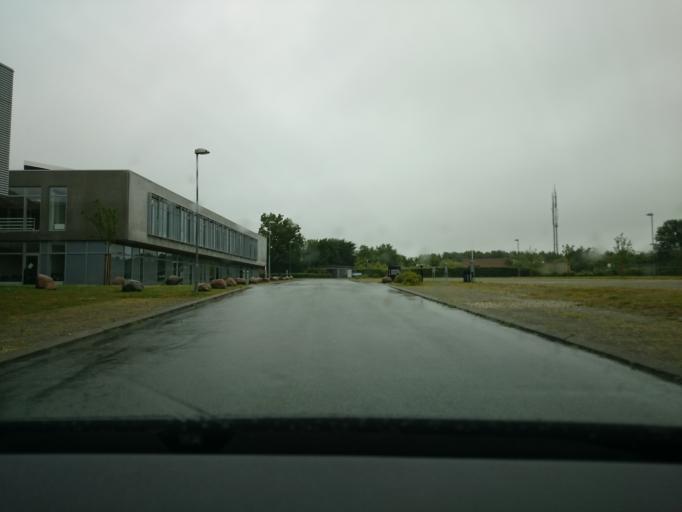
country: DK
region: Central Jutland
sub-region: Randers Kommune
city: Randers
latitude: 56.4312
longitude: 10.0686
